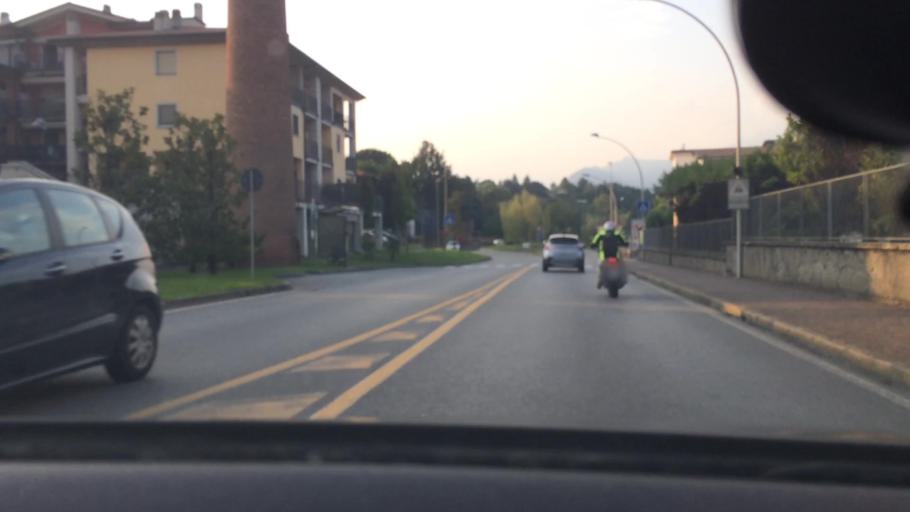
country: IT
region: Lombardy
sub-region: Provincia di Lecco
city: Brivio
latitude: 45.7411
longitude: 9.4459
